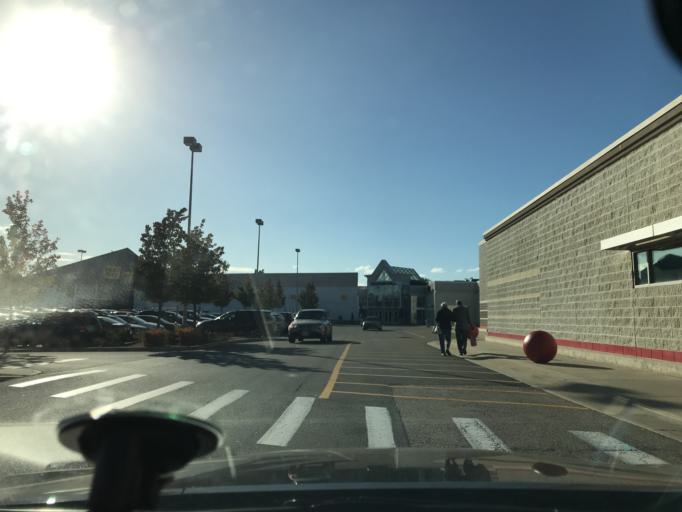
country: US
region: Massachusetts
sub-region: Middlesex County
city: Watertown
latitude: 42.3641
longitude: -71.1573
